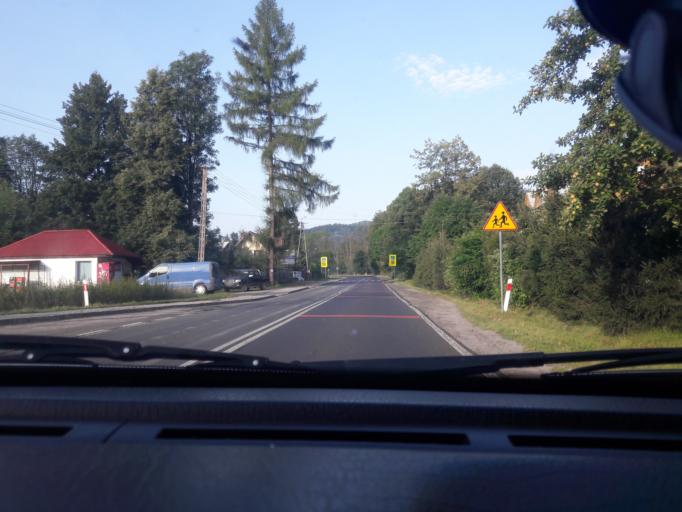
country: PL
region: Lesser Poland Voivodeship
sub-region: Powiat suski
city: Zawoja
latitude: 49.6437
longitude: 19.5416
